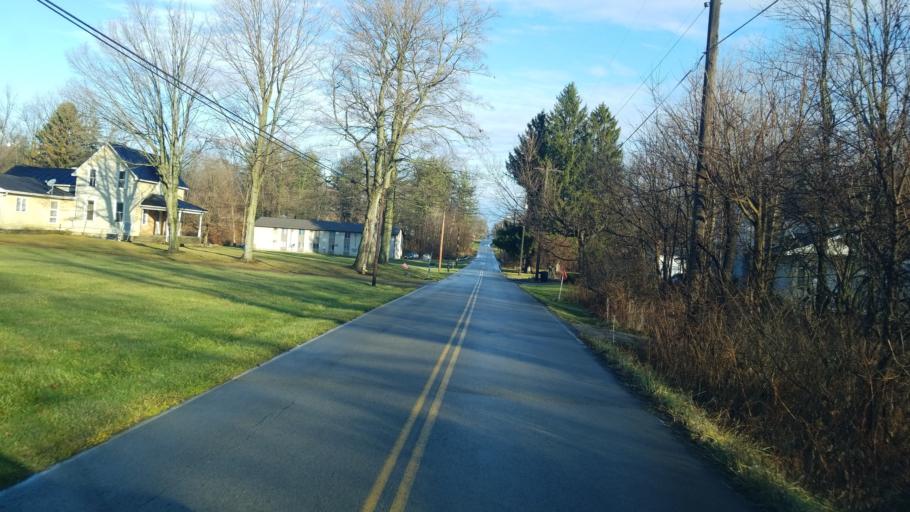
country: US
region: Ohio
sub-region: Richland County
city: Mansfield
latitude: 40.7289
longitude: -82.5036
